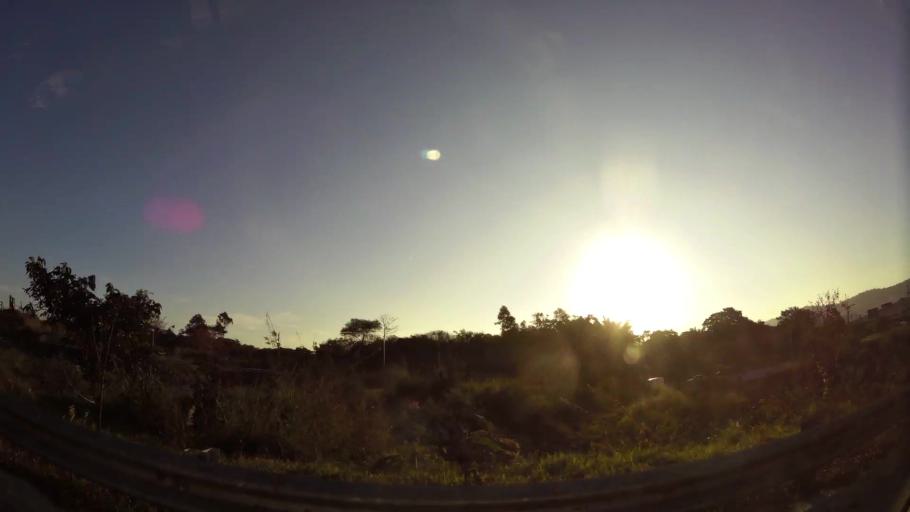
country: SV
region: La Libertad
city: Santa Tecla
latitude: 13.6826
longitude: -89.2639
